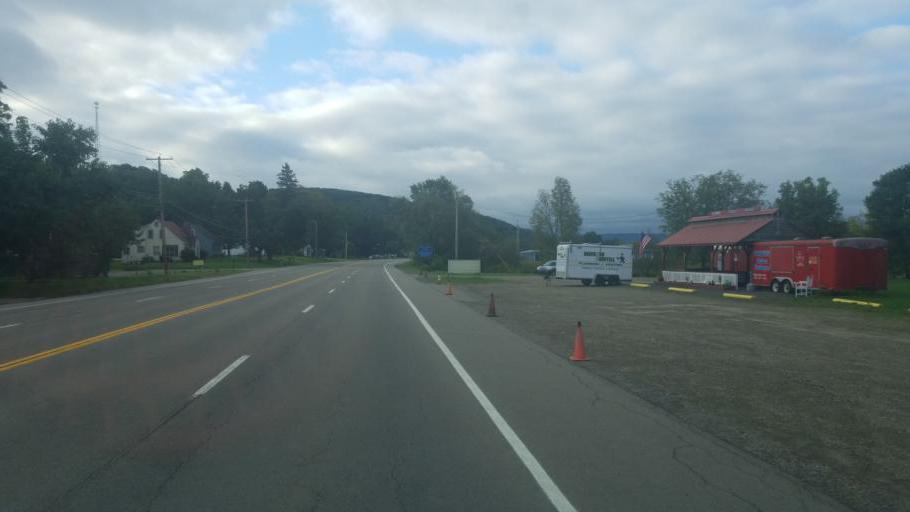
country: US
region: New York
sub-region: Cattaraugus County
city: Olean
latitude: 42.1182
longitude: -78.4152
